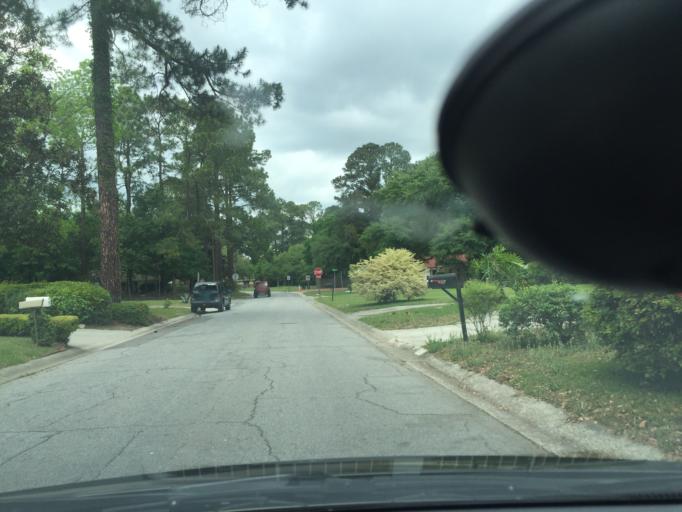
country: US
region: Georgia
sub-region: Chatham County
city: Montgomery
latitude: 31.9923
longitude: -81.1239
